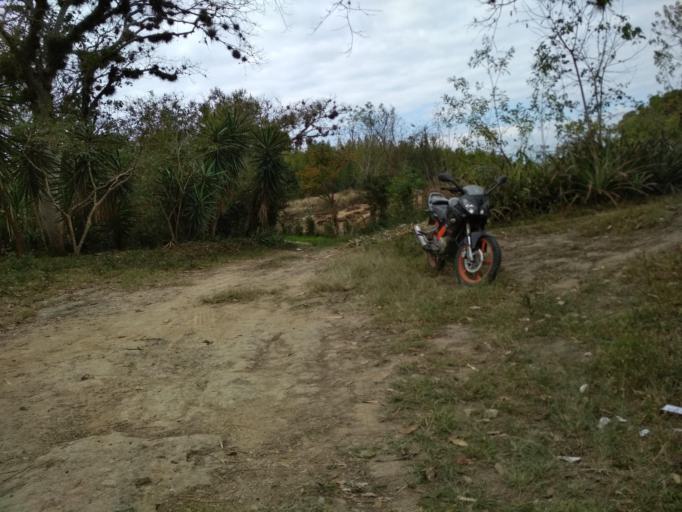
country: MX
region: Veracruz
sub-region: Coatepec
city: Tuzamapan
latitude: 19.3663
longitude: -96.8818
